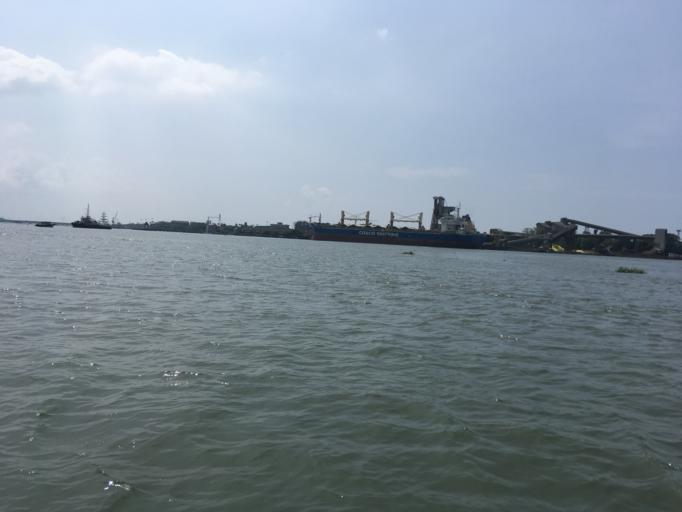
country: IN
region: Kerala
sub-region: Ernakulam
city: Cochin
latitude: 9.9701
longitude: 76.2747
